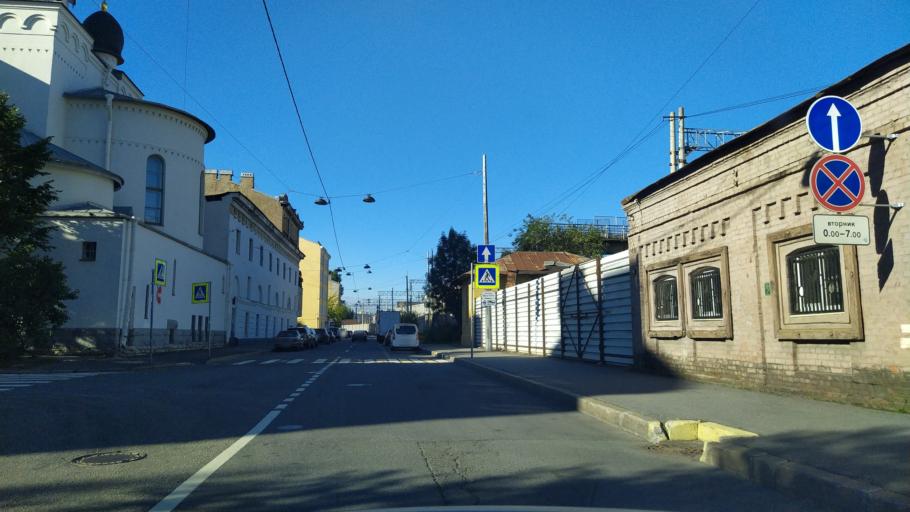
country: RU
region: St.-Petersburg
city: Centralniy
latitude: 59.9178
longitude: 30.3625
